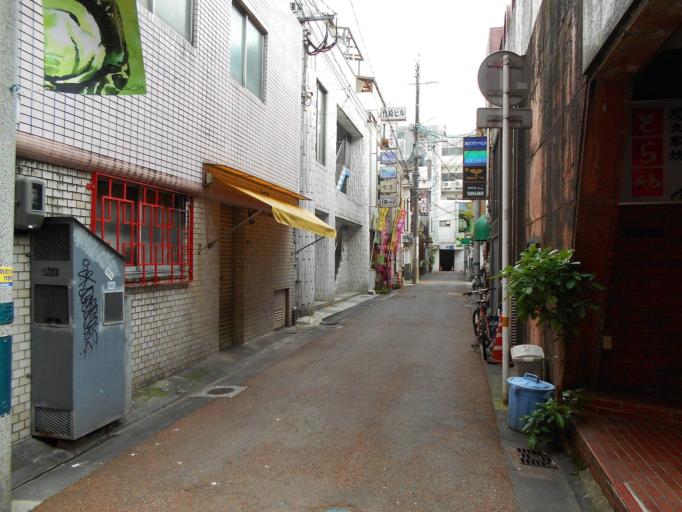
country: JP
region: Miyazaki
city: Miyazaki-shi
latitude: 31.9141
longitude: 131.4218
